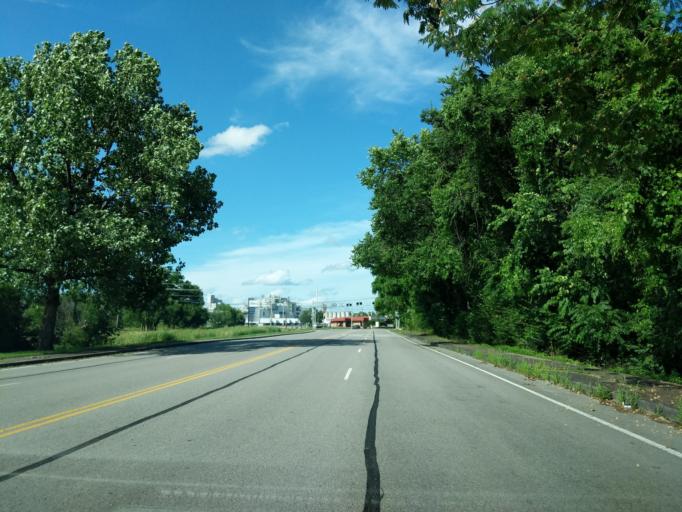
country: US
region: Tennessee
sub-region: Davidson County
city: Lakewood
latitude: 36.2655
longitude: -86.6581
